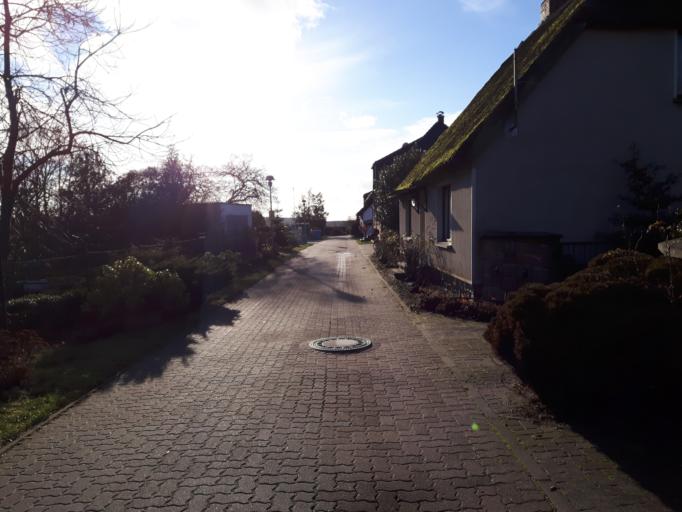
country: DE
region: Mecklenburg-Vorpommern
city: Ostseebad Sellin
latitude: 54.3528
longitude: 13.6841
